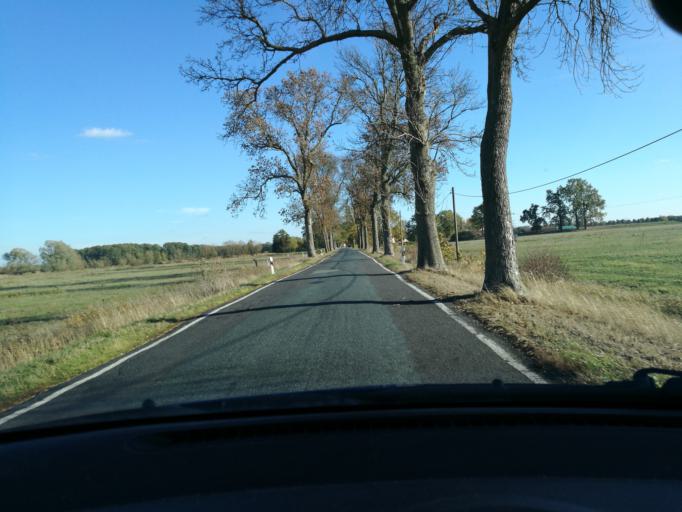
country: DE
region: Brandenburg
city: Lenzen
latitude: 53.1099
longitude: 11.4124
